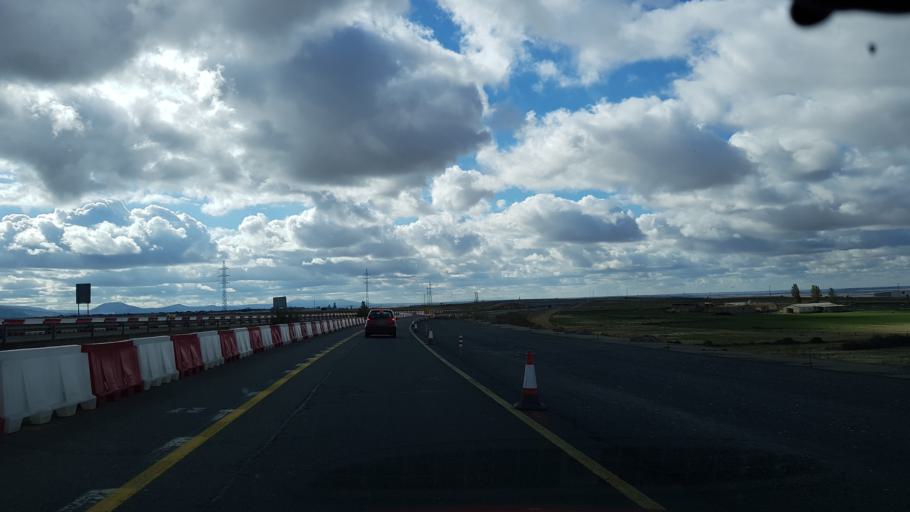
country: ES
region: Castille and Leon
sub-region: Provincia de Segovia
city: Palazuelos de Eresma
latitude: 40.9233
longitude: -4.0920
